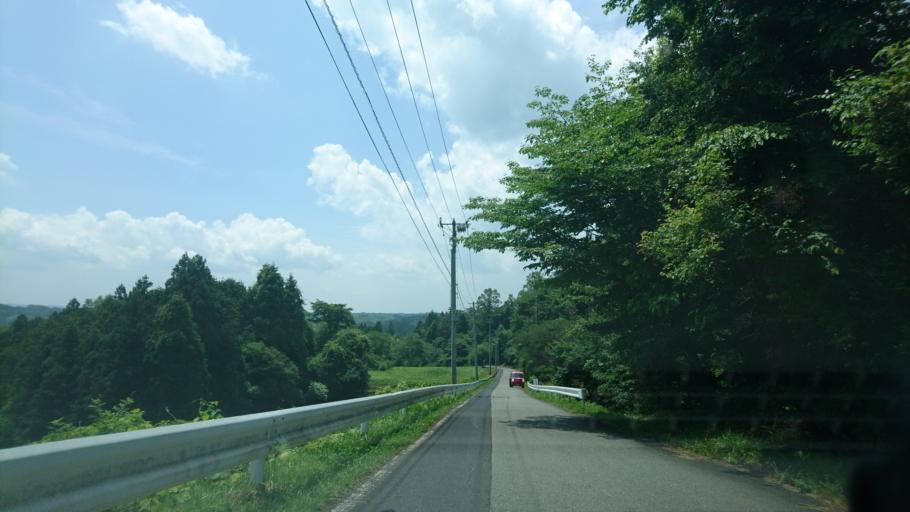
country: JP
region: Iwate
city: Ichinoseki
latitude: 38.9178
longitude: 141.2225
